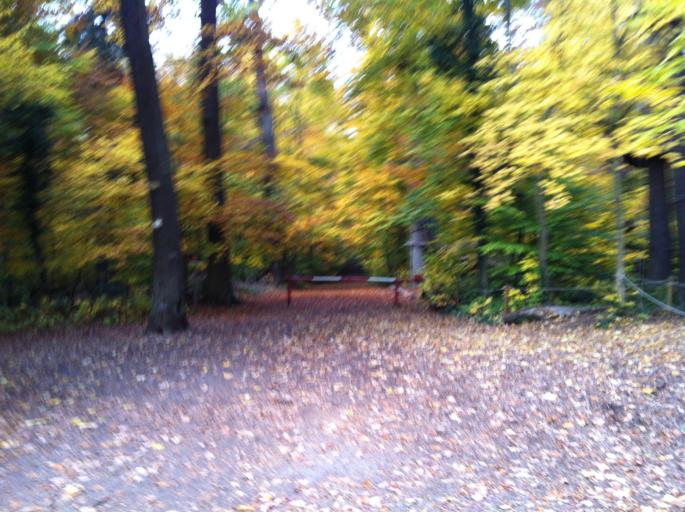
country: DE
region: Hesse
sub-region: Regierungsbezirk Darmstadt
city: Wiesbaden
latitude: 50.0996
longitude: 8.2302
